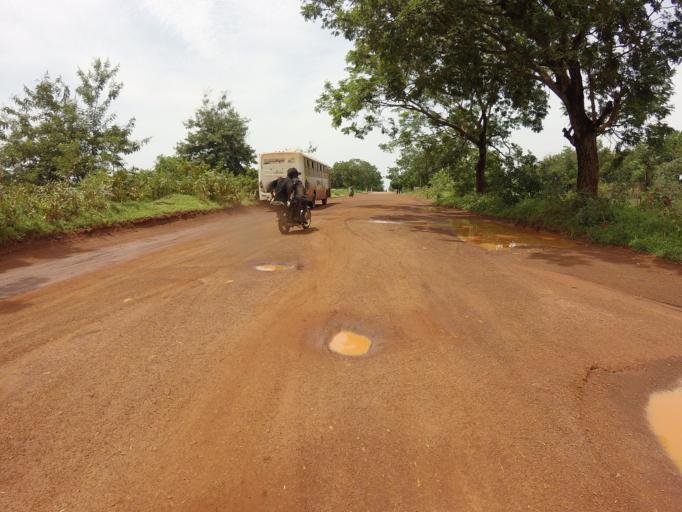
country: GH
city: Kpandae
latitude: 8.8713
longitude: 0.0452
